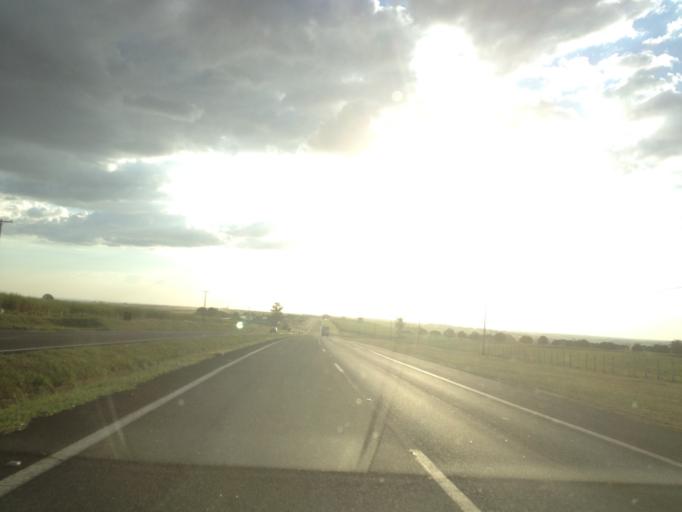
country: BR
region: Sao Paulo
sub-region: Jau
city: Jau
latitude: -22.2711
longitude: -48.4730
